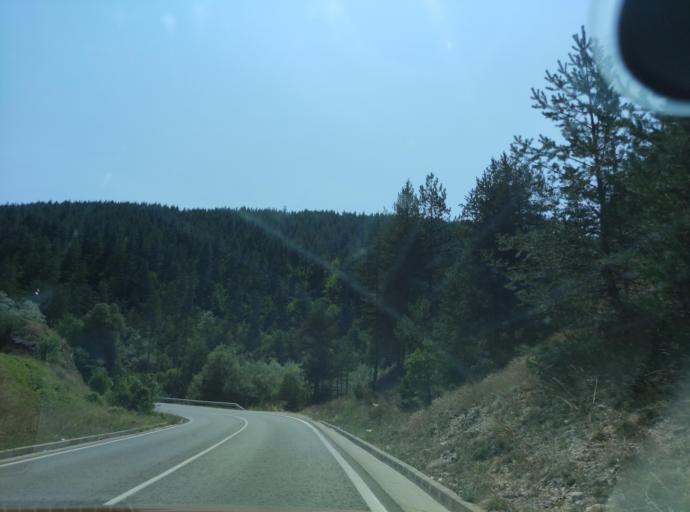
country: BG
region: Blagoevgrad
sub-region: Obshtina Belitsa
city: Belitsa
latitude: 41.8940
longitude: 23.5426
